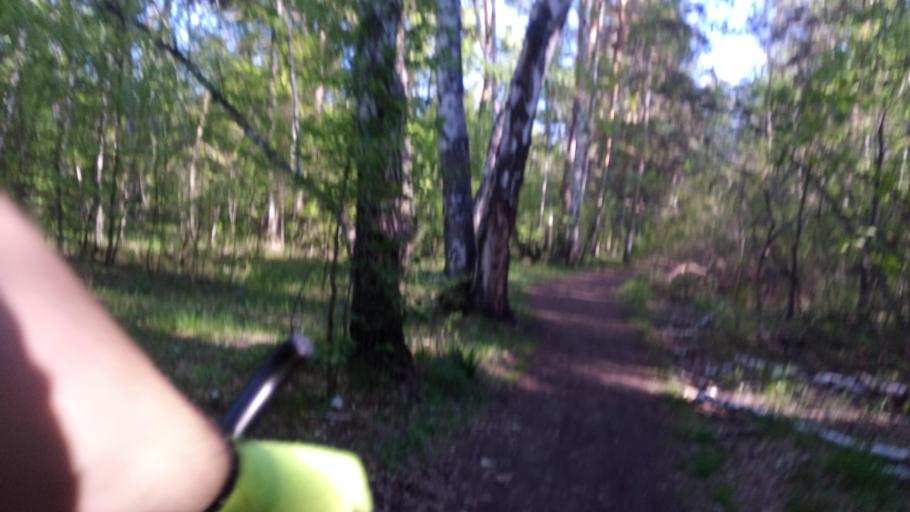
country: RU
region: Chelyabinsk
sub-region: Gorod Chelyabinsk
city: Chelyabinsk
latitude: 55.1424
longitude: 61.3394
